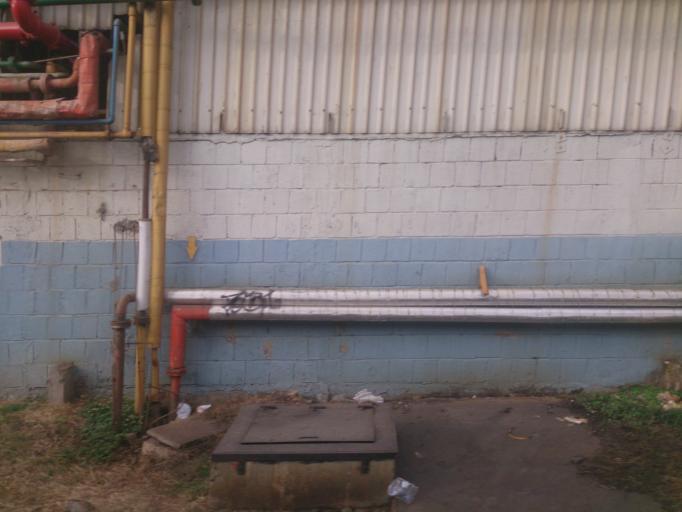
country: CR
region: San Jose
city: San Jose
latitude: 9.9258
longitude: -84.0904
